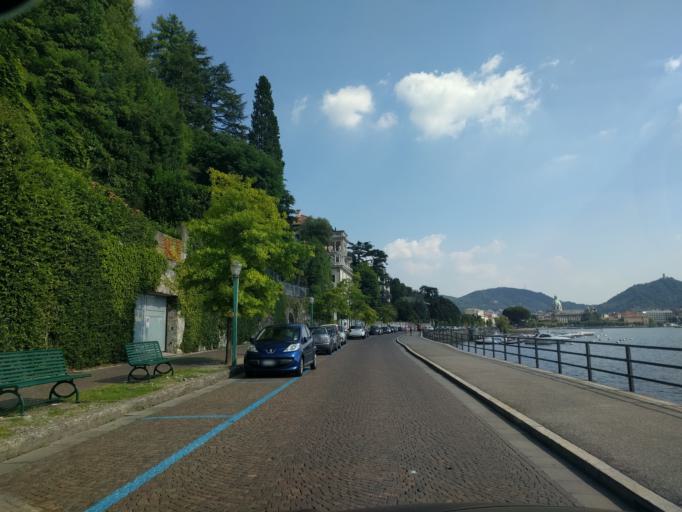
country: IT
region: Lombardy
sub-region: Provincia di Como
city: Brunate
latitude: 45.8219
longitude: 9.0787
